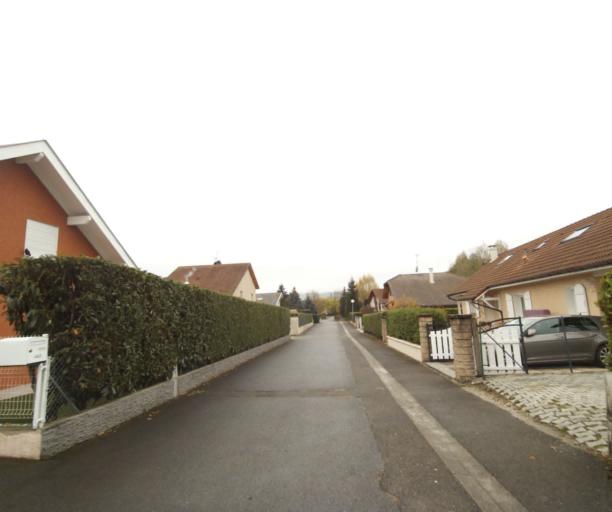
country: FR
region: Rhone-Alpes
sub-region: Departement de la Haute-Savoie
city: Reignier-Esery
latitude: 46.1351
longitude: 6.2837
